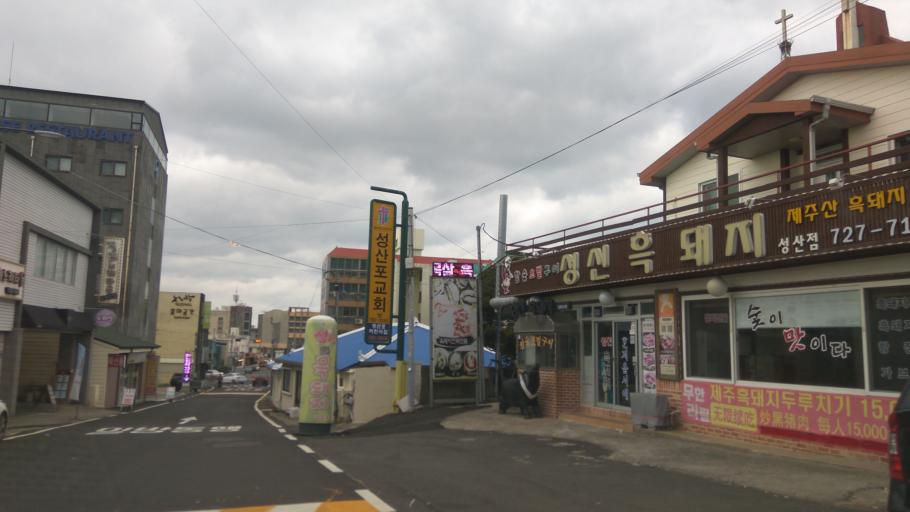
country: KR
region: Jeju-do
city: Jeju-si
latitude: 33.4635
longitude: 126.9350
